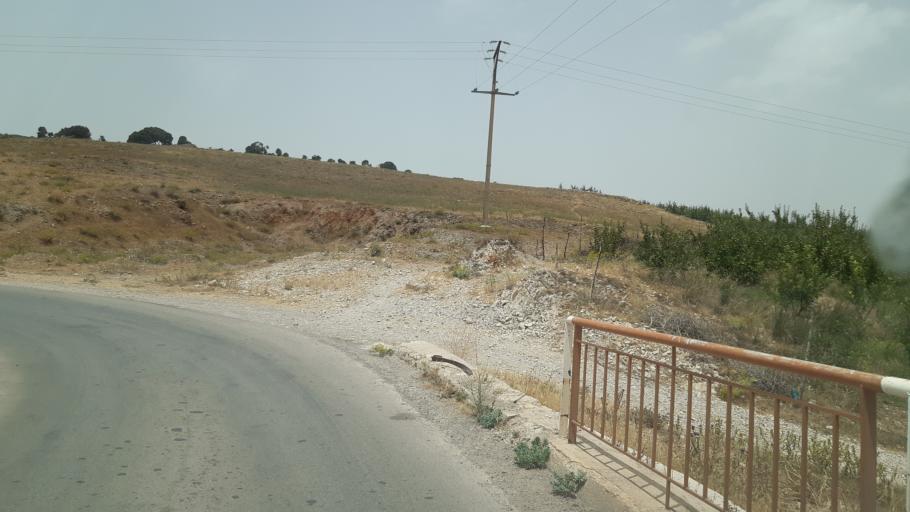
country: MA
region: Meknes-Tafilalet
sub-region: Ifrane
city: Ifrane
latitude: 33.6537
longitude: -5.0137
